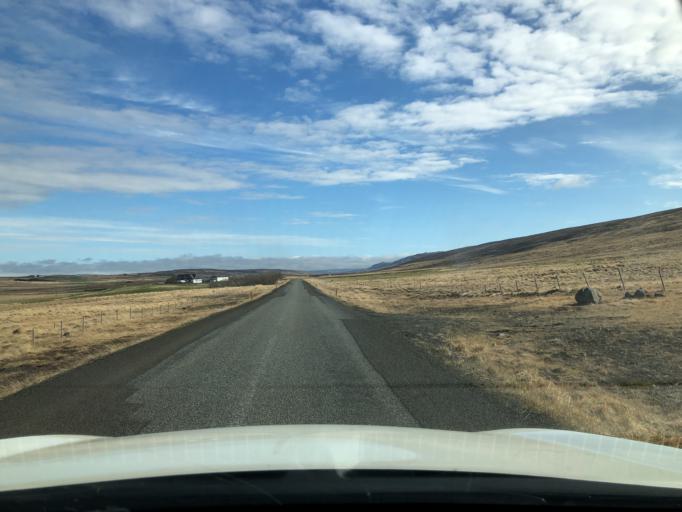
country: IS
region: West
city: Borgarnes
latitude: 65.0932
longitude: -21.7275
